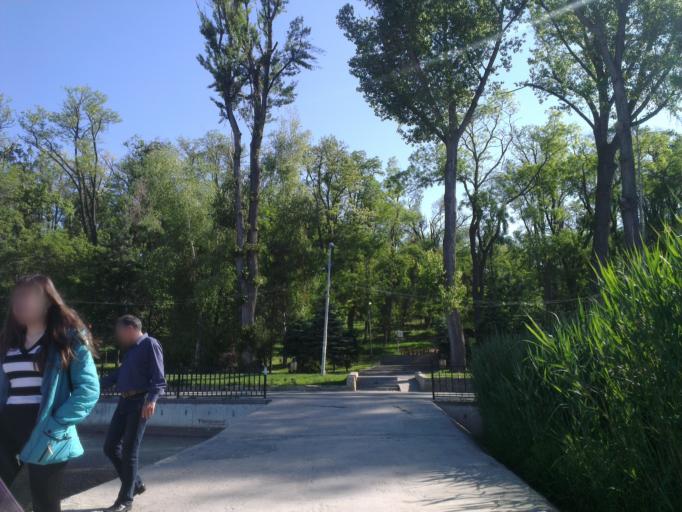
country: MD
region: Chisinau
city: Chisinau
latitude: 47.0191
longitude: 28.8176
